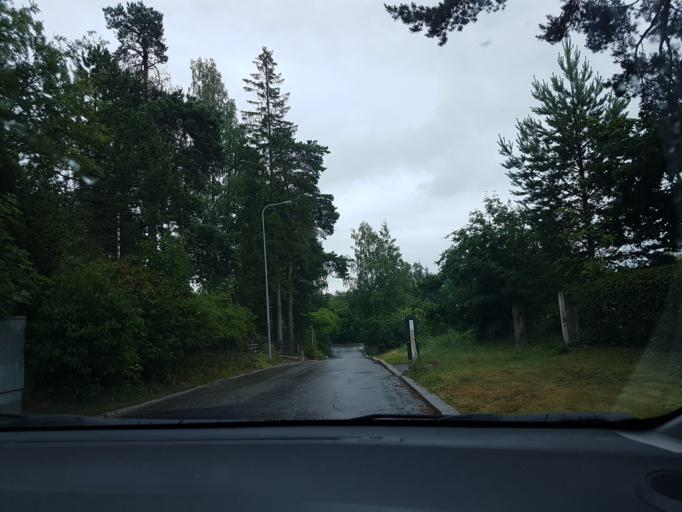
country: FI
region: Uusimaa
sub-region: Helsinki
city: Vantaa
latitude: 60.2303
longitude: 25.0968
